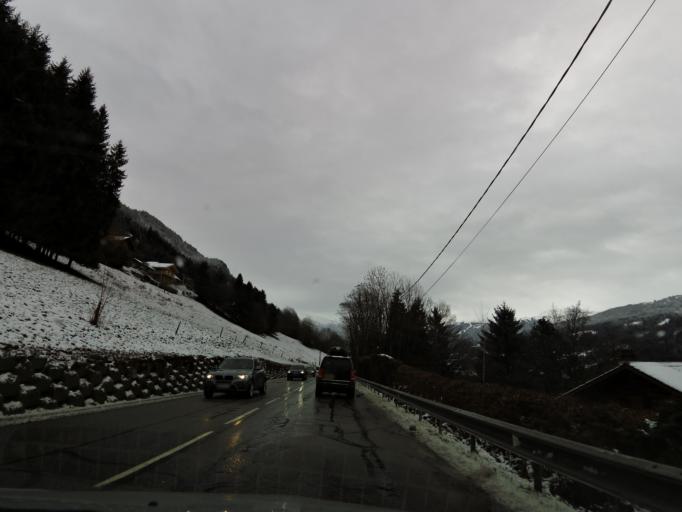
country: FR
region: Rhone-Alpes
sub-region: Departement de la Haute-Savoie
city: Taninges
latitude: 46.1112
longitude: 6.6107
